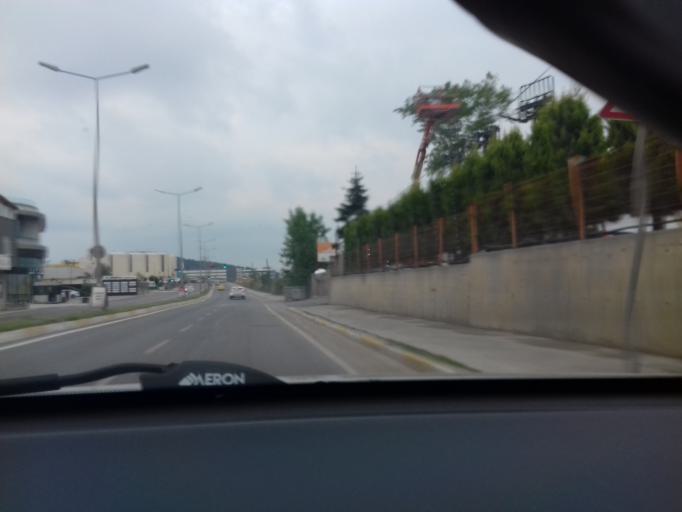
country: TR
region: Istanbul
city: Icmeler
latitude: 40.8907
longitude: 29.3539
